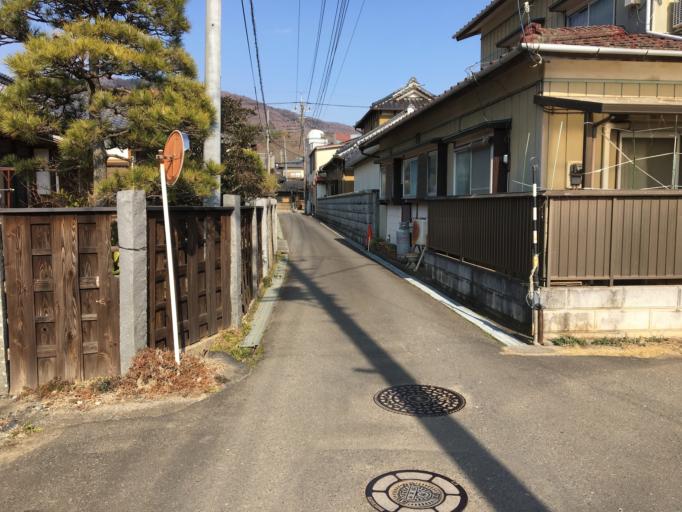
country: JP
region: Ibaraki
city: Tsukuba
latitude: 36.1525
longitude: 140.1134
